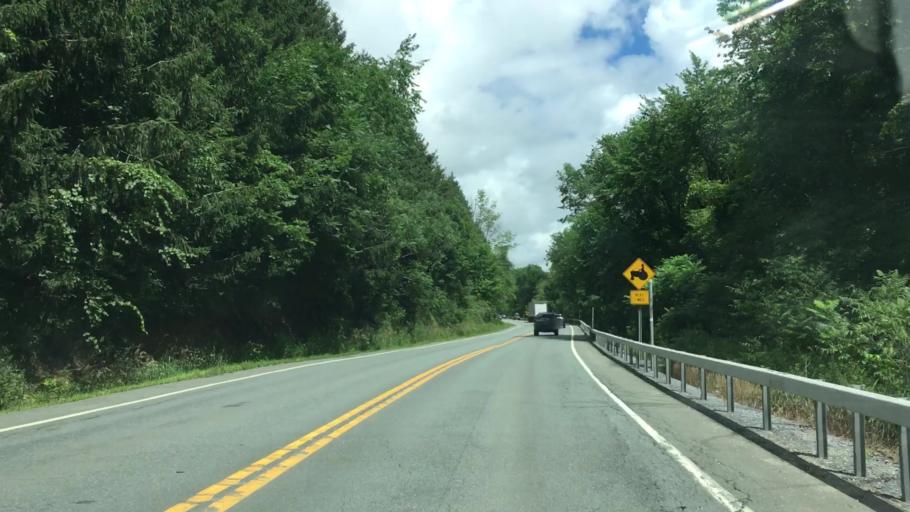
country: US
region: New York
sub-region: Rensselaer County
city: Hoosick Falls
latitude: 42.8729
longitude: -73.3085
